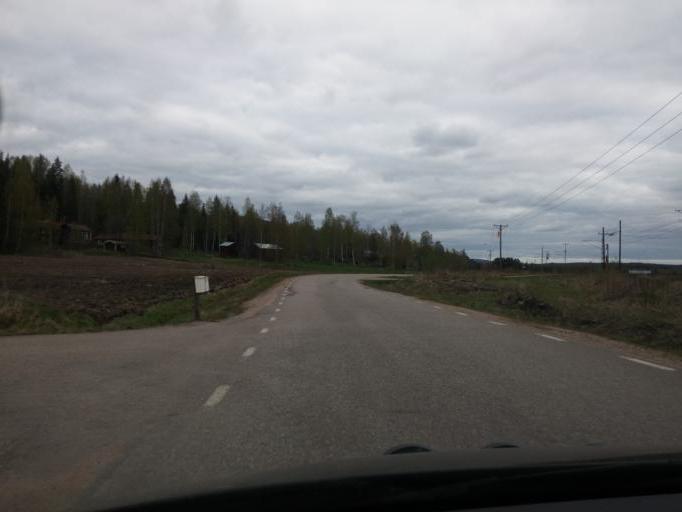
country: SE
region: Gaevleborg
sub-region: Ljusdals Kommun
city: Ljusdal
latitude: 61.8485
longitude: 16.0580
